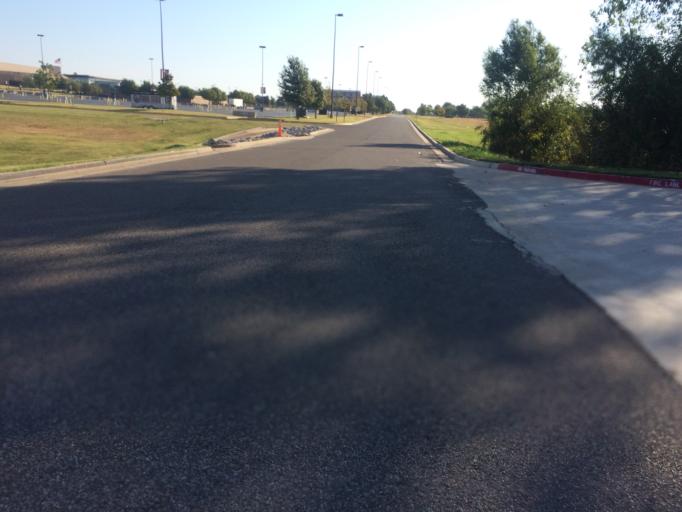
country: US
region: Oklahoma
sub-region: Cleveland County
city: Norman
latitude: 35.1852
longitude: -97.4478
